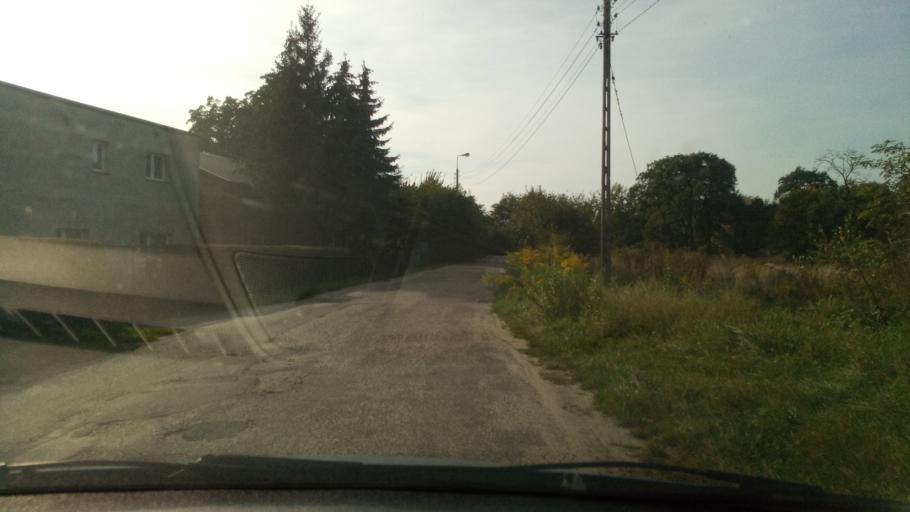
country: PL
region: Silesian Voivodeship
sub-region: Sosnowiec
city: Sosnowiec
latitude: 50.2620
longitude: 19.1289
